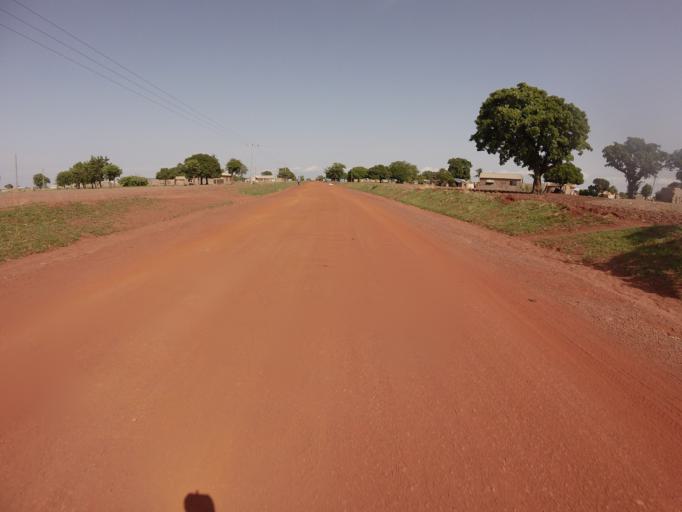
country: GH
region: Upper East
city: Bawku
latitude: 10.8351
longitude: -0.1749
